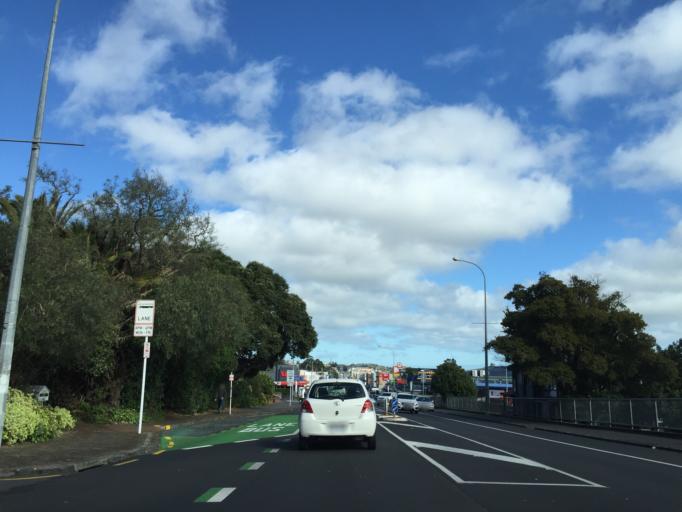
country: NZ
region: Auckland
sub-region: Auckland
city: Auckland
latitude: -36.8738
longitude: 174.7518
